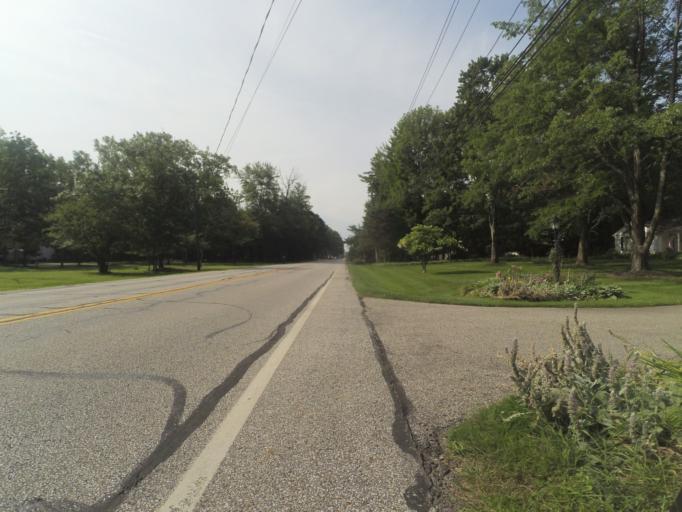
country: US
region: Ohio
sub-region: Cuyahoga County
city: Orange
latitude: 41.4533
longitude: -81.4803
